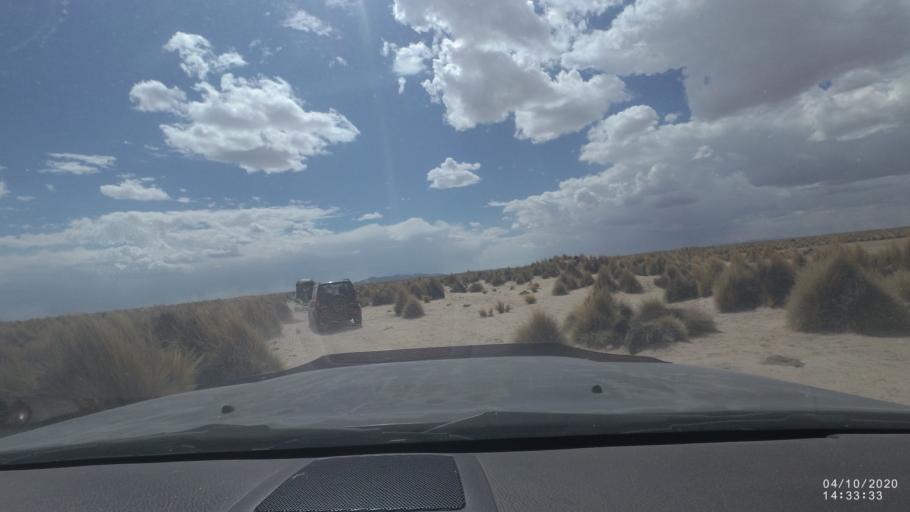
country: BO
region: Oruro
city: Poopo
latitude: -18.6711
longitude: -67.4672
